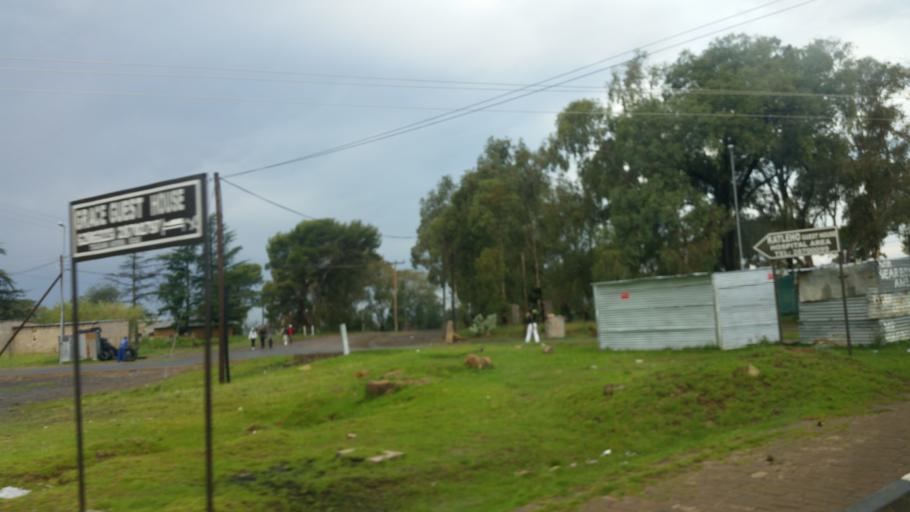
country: LS
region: Mafeteng
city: Mafeteng
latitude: -29.8193
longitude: 27.2373
